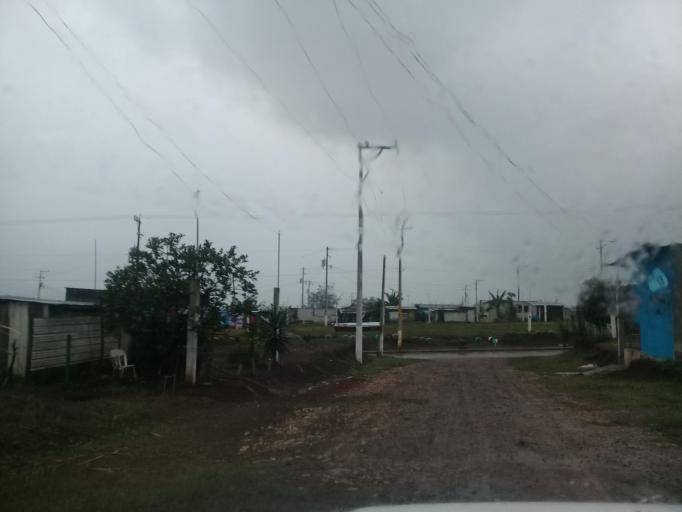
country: MX
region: Veracruz
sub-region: Cordoba
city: San Jose de Tapia
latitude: 18.8516
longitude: -96.9563
